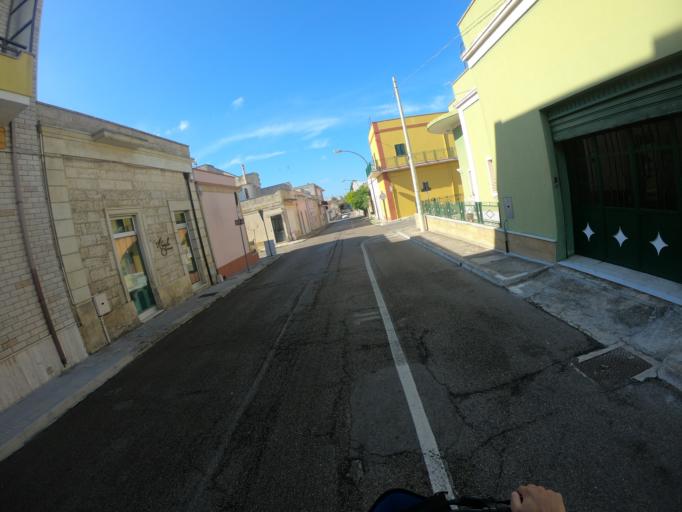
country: IT
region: Apulia
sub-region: Provincia di Lecce
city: Supersano
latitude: 40.0146
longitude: 18.2412
